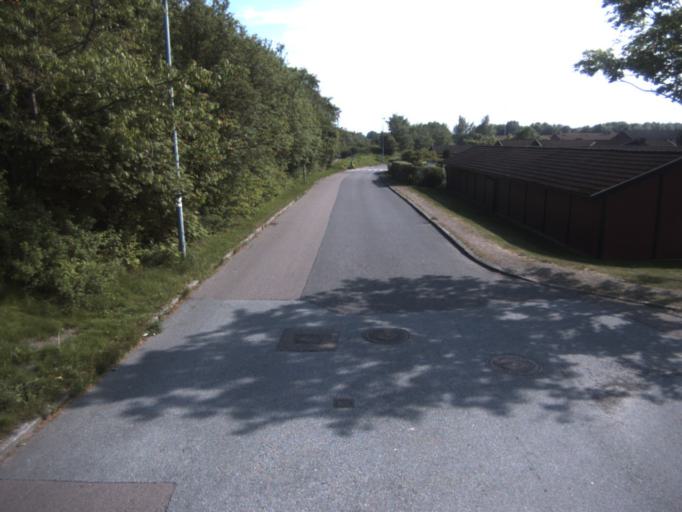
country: SE
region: Skane
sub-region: Helsingborg
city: Helsingborg
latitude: 56.0709
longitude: 12.6997
